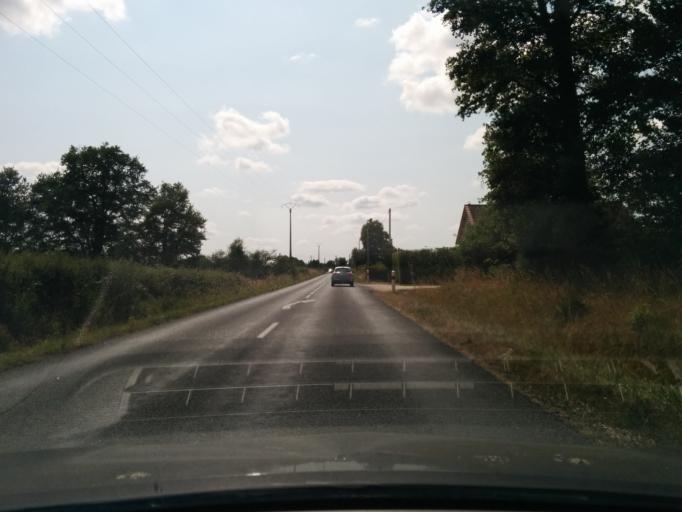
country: FR
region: Centre
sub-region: Departement du Cher
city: Vierzon
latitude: 47.2503
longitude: 2.1029
